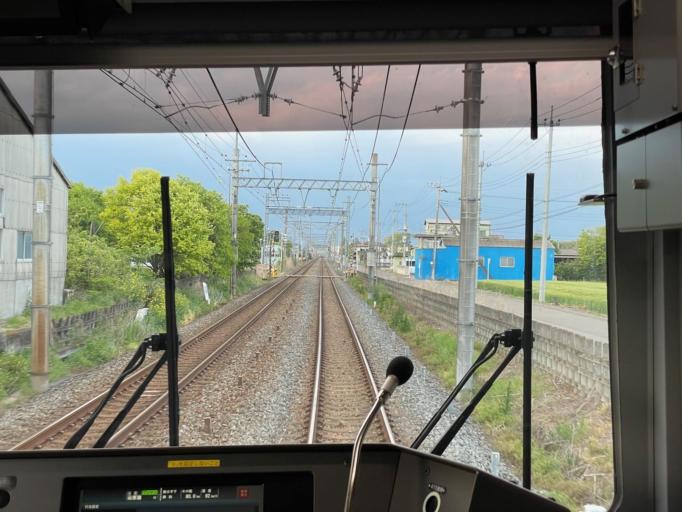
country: JP
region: Tochigi
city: Tochigi
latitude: 36.3287
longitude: 139.6965
